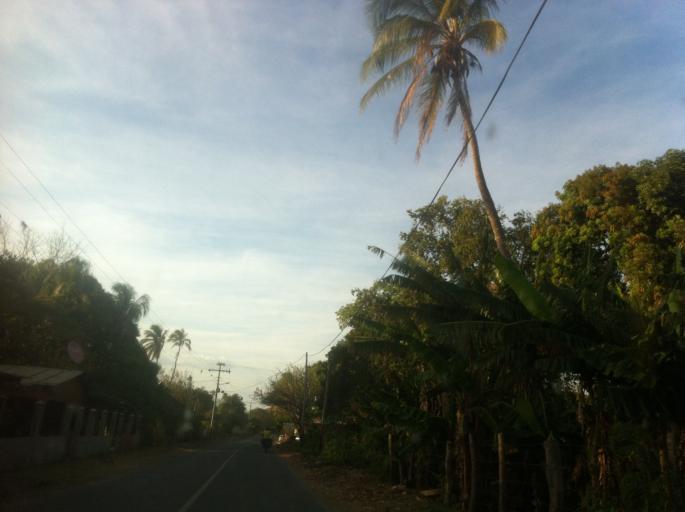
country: NI
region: Rivas
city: Buenos Aires
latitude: 11.4666
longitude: -85.8447
